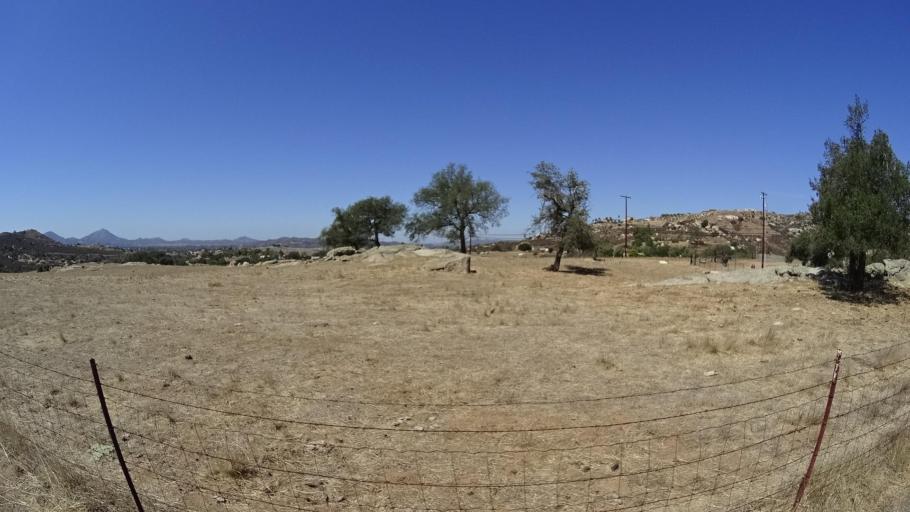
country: US
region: California
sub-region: San Diego County
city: Ramona
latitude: 33.0438
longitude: -116.8237
